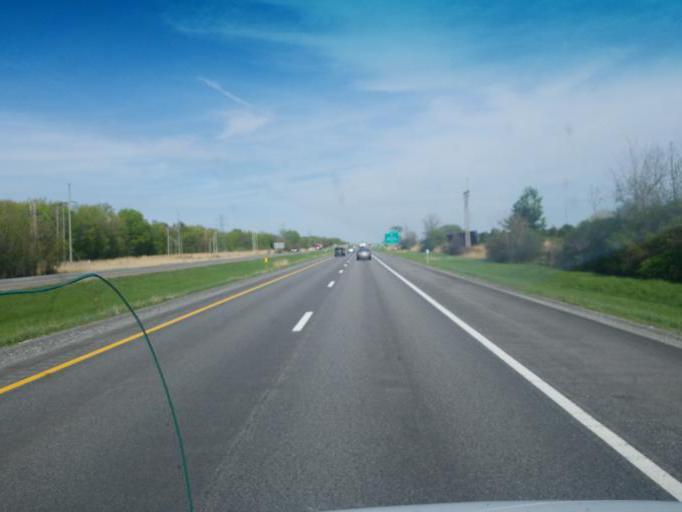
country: US
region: New York
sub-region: Onondaga County
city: East Syracuse
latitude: 43.0940
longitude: -76.0711
